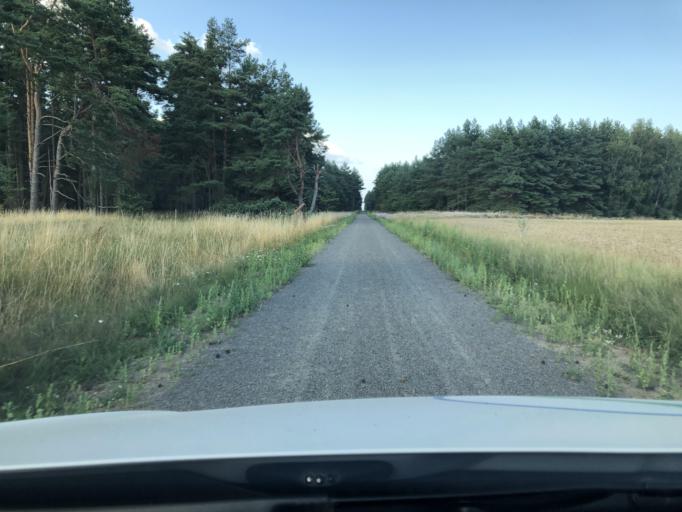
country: SE
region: Skane
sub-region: Kristianstads Kommun
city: Norra Asum
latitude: 55.9224
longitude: 14.1245
